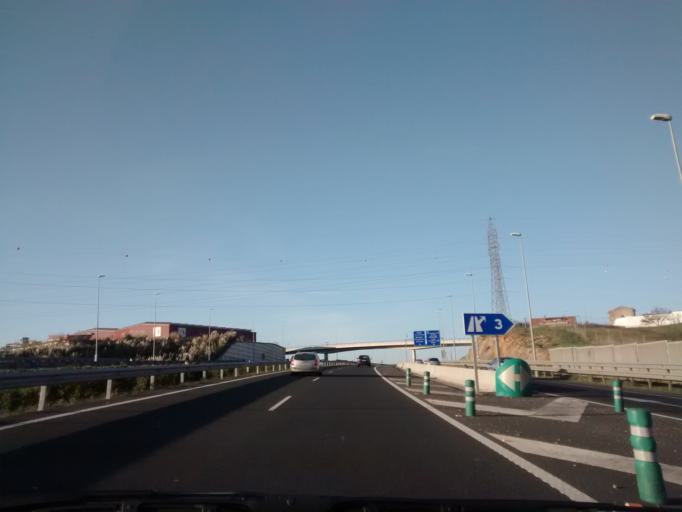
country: ES
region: Cantabria
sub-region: Provincia de Cantabria
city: Camargo
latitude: 43.4330
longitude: -3.8755
